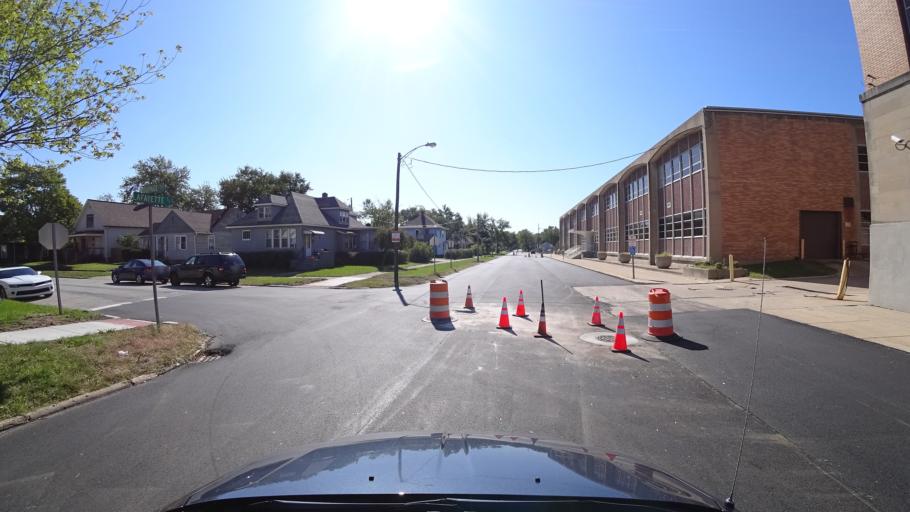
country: US
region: Indiana
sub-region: LaPorte County
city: Michigan City
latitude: 41.7100
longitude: -86.8938
